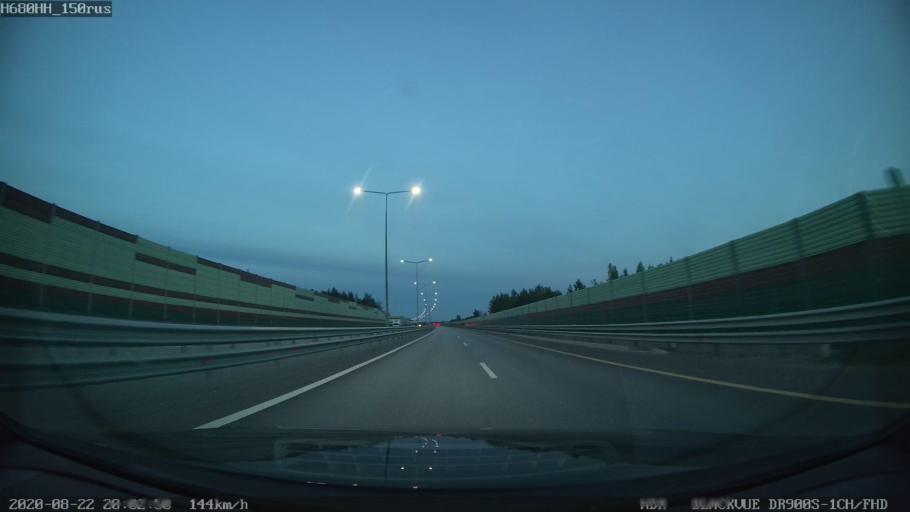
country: RU
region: Tverskaya
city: Radchenko
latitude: 56.6640
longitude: 36.3484
